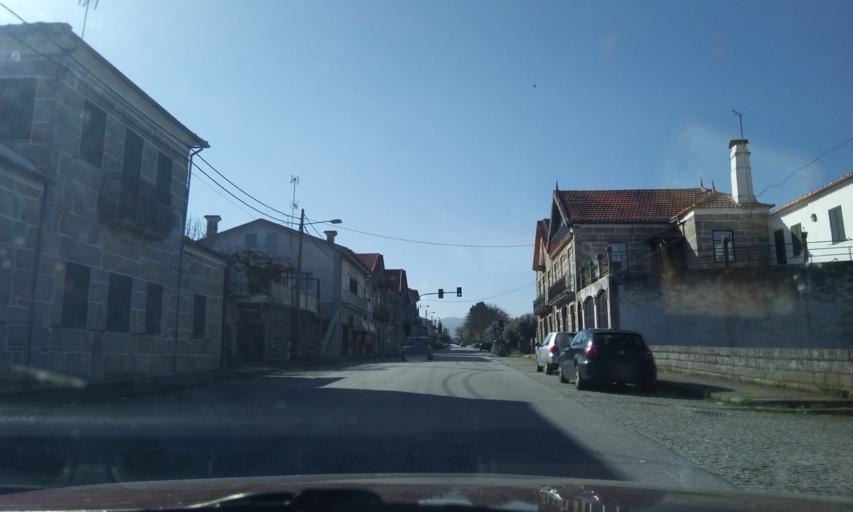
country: PT
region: Guarda
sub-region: Celorico da Beira
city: Celorico da Beira
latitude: 40.6647
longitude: -7.3815
